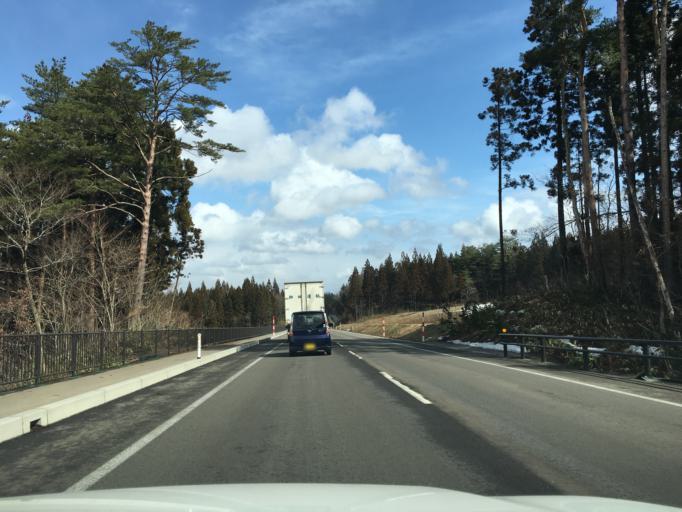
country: JP
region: Akita
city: Takanosu
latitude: 40.1090
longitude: 140.3569
